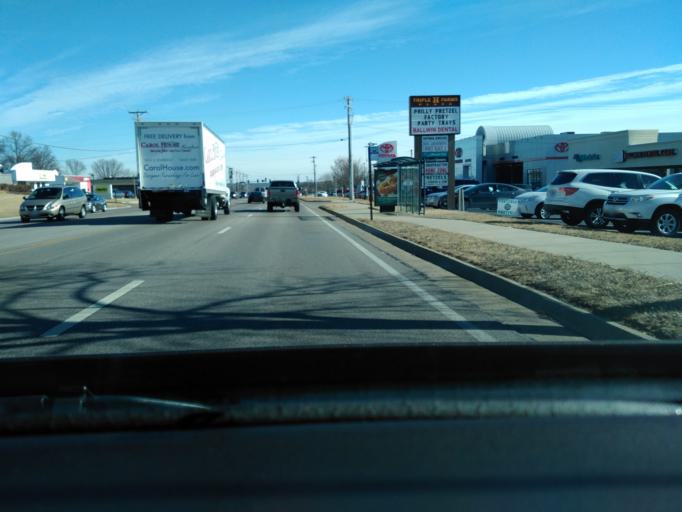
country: US
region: Missouri
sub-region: Saint Louis County
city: Winchester
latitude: 38.5929
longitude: -90.5329
